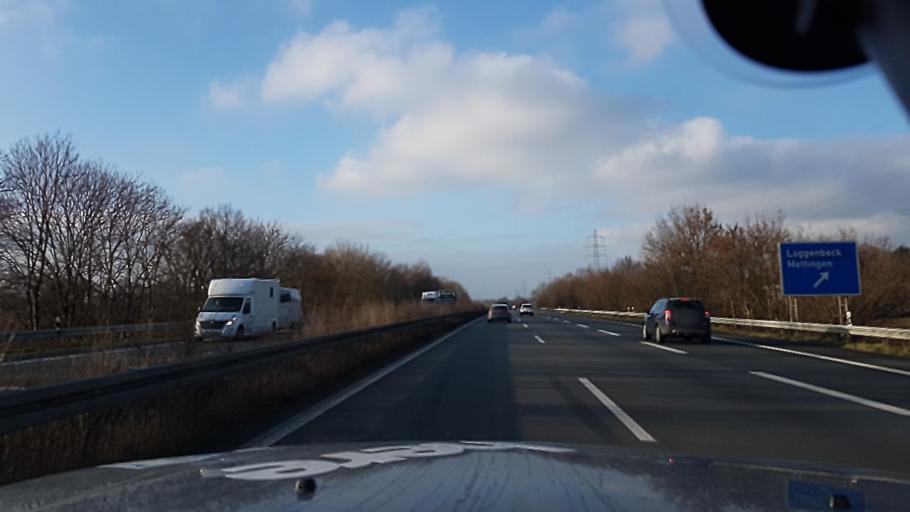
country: DE
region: North Rhine-Westphalia
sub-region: Regierungsbezirk Munster
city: Tecklenburg
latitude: 52.2546
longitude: 7.7813
